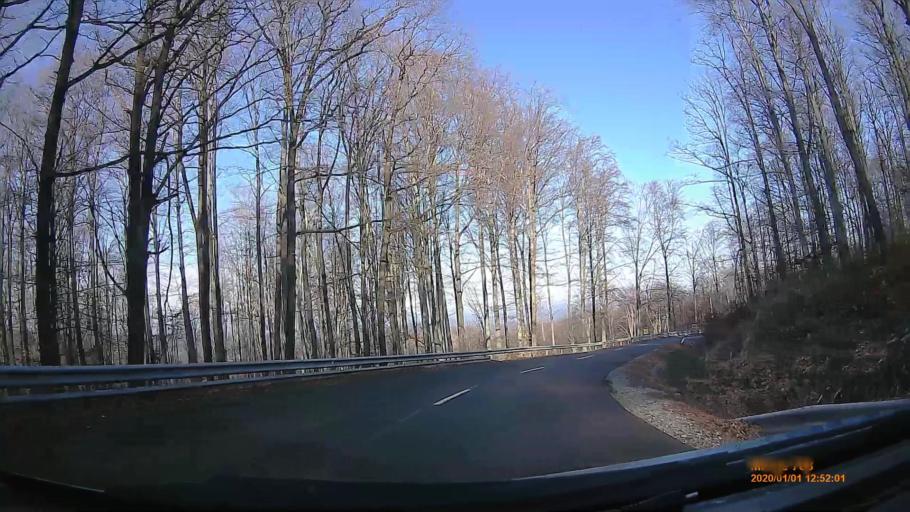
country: HU
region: Heves
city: Paradsasvar
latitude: 47.8988
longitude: 19.9855
